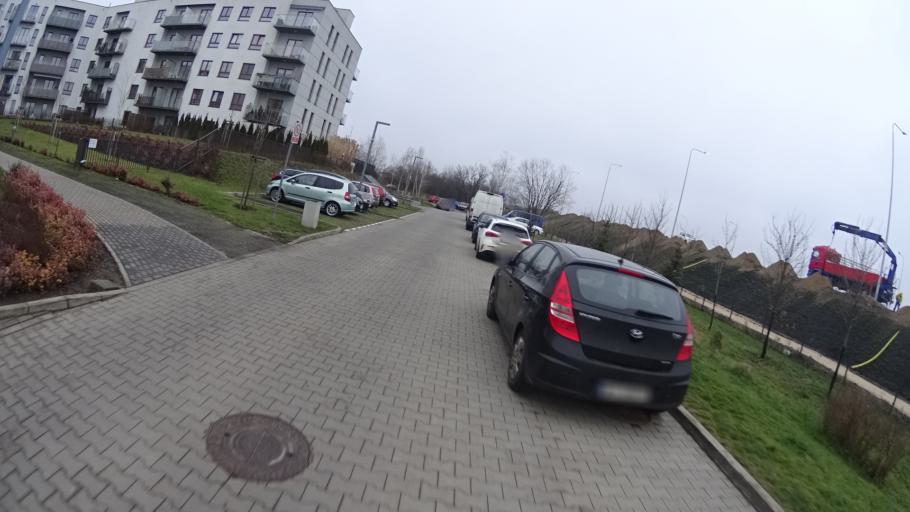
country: PL
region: Masovian Voivodeship
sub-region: Warszawa
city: Wilanow
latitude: 52.1531
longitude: 21.0810
